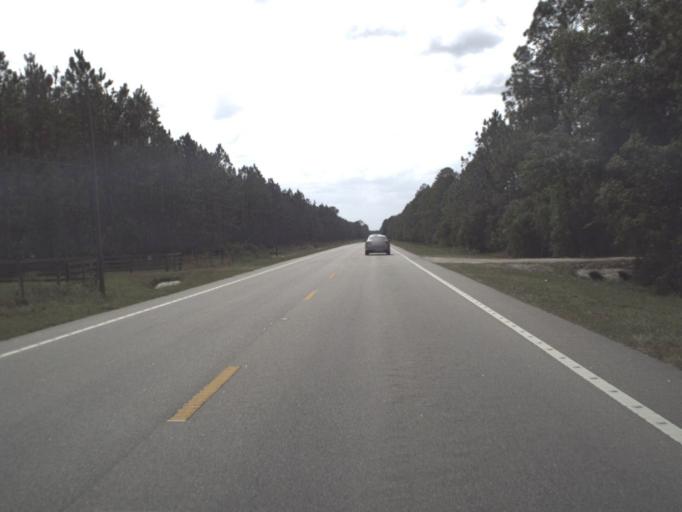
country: US
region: Florida
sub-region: Putnam County
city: Crescent City
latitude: 29.4809
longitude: -81.4256
